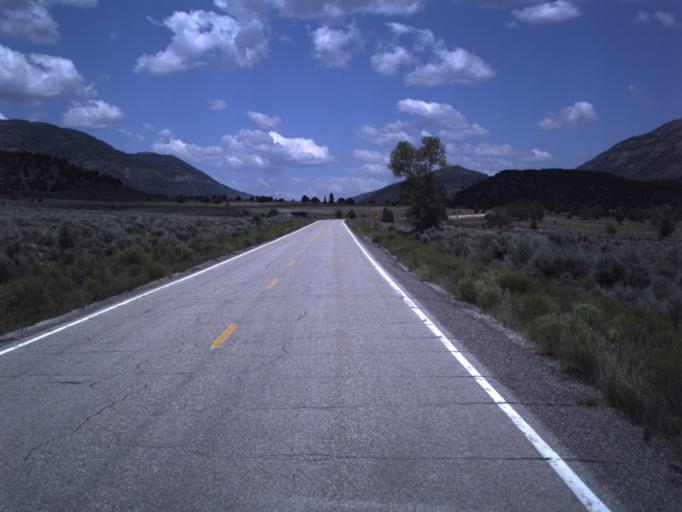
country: US
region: Utah
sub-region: Emery County
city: Orangeville
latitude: 39.3190
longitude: -111.2826
